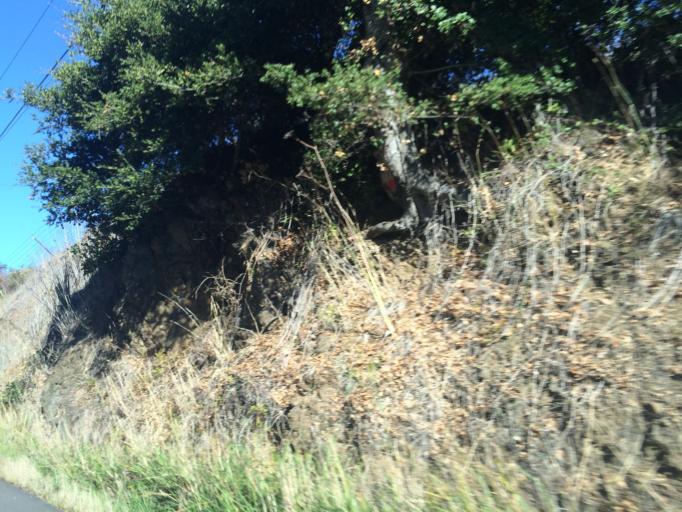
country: US
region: California
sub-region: Marin County
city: Lagunitas-Forest Knolls
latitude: 38.0364
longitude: -122.7452
